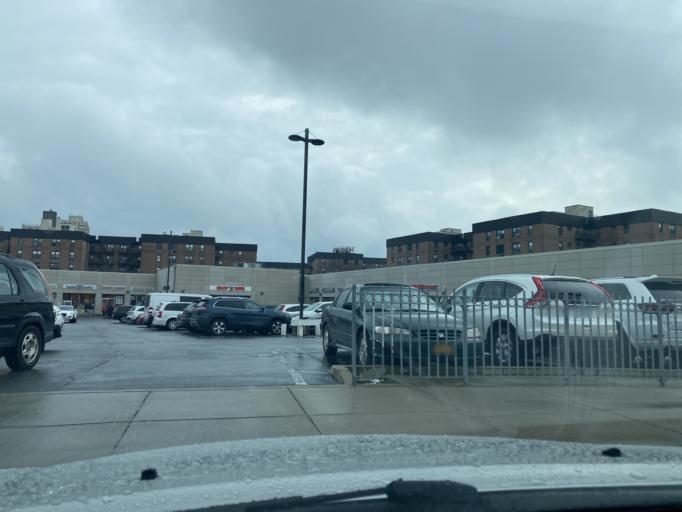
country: US
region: New York
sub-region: Nassau County
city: Inwood
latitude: 40.5971
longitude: -73.7548
